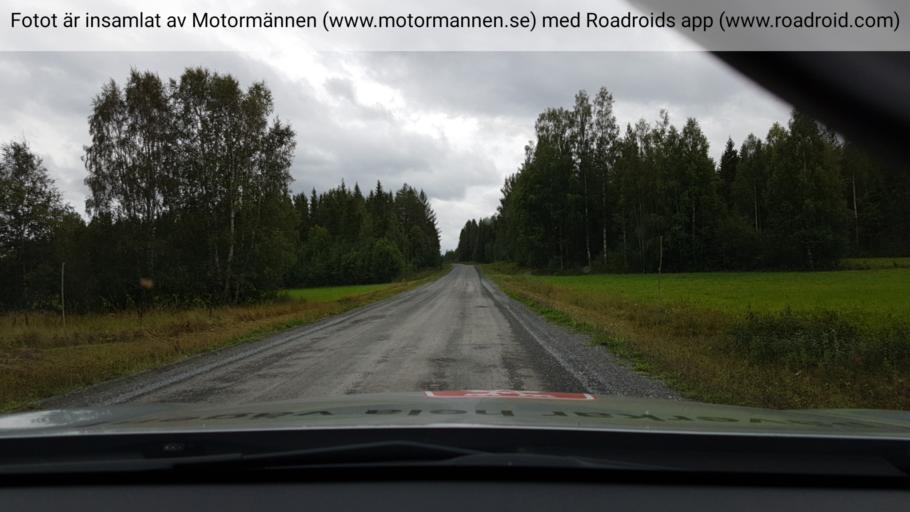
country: SE
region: Vaesterbotten
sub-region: Skelleftea Kommun
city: Forsbacka
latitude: 64.8126
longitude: 20.4947
